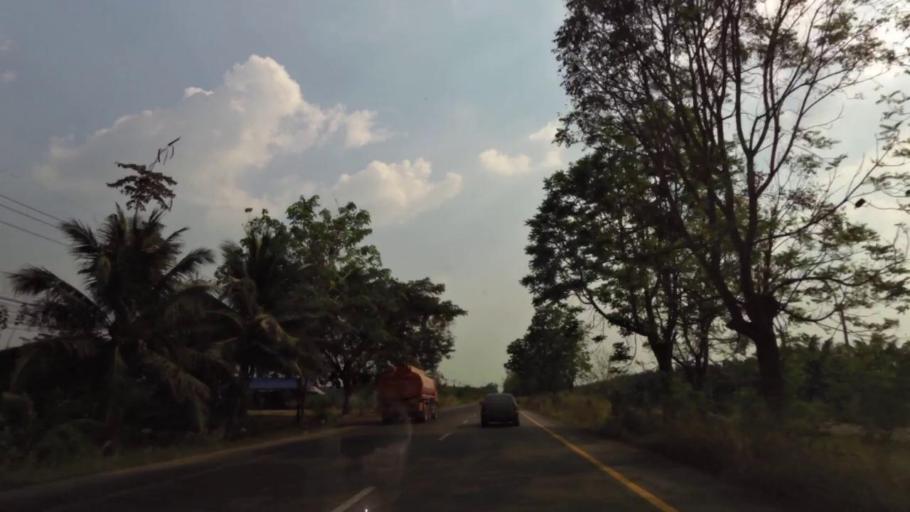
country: TH
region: Rayong
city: Wang Chan
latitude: 13.0007
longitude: 101.4833
